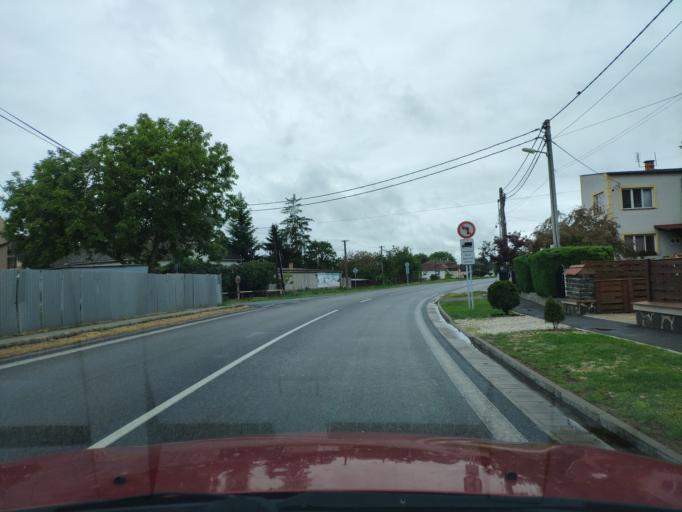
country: HU
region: Borsod-Abauj-Zemplen
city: Ricse
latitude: 48.4319
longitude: 21.9175
